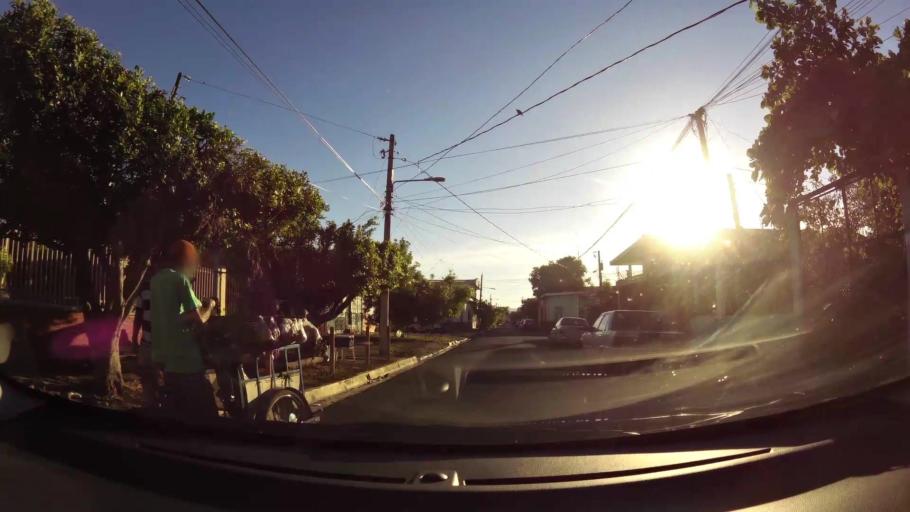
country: SV
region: San Miguel
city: San Miguel
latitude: 13.4868
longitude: -88.1819
